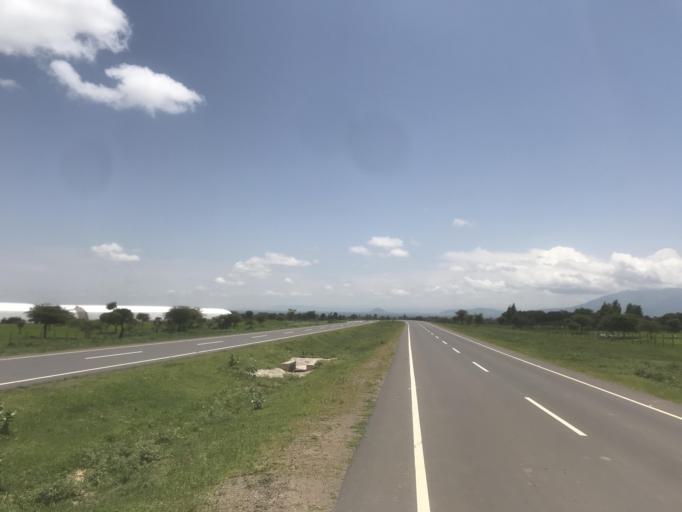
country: ET
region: Oromiya
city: Mojo
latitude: 8.5069
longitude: 39.0714
